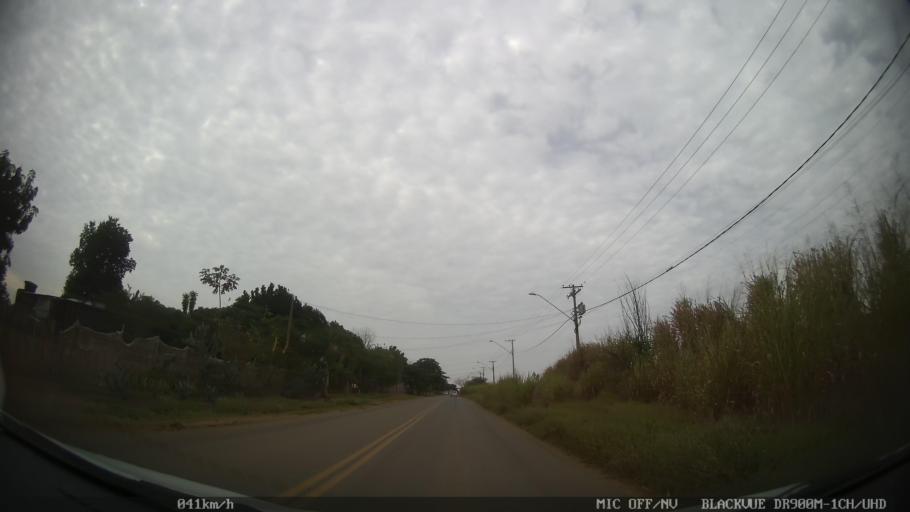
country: BR
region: Sao Paulo
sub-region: Cosmopolis
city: Cosmopolis
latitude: -22.6899
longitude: -47.2354
